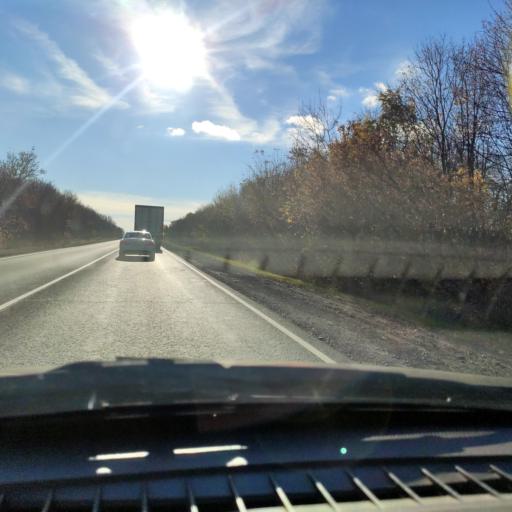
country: RU
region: Samara
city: Zhigulevsk
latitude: 53.3135
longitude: 49.3598
